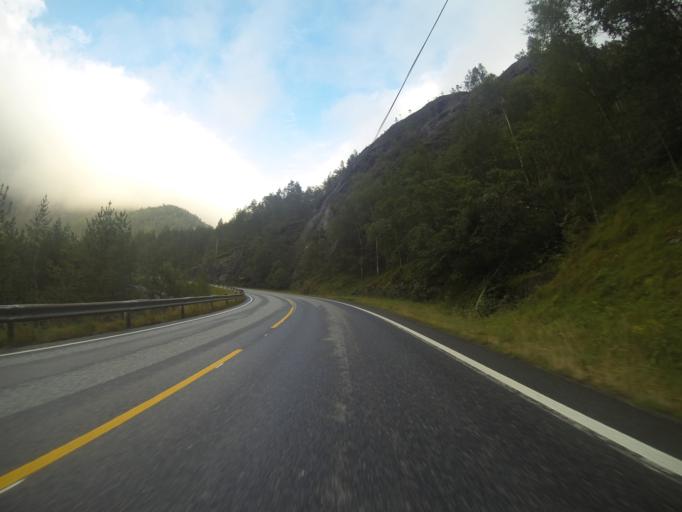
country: NO
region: Rogaland
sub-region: Sauda
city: Sauda
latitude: 59.8738
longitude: 6.4016
